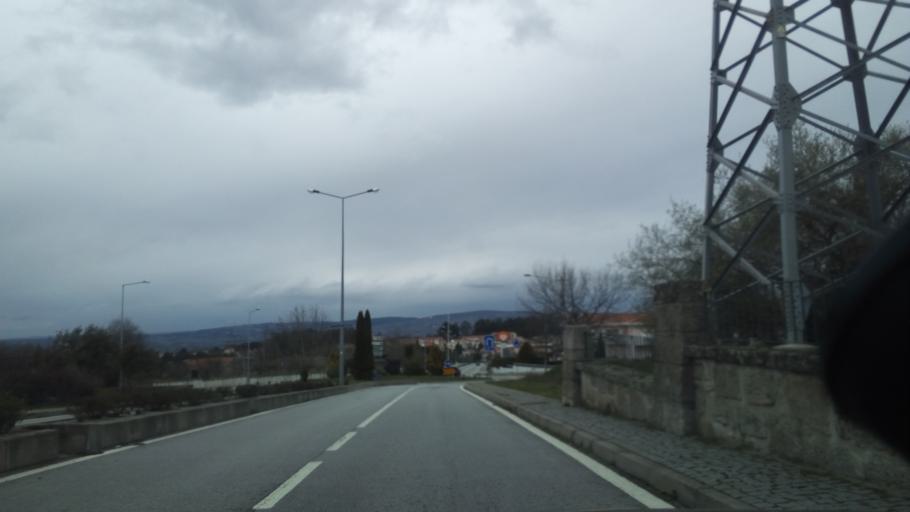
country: PT
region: Guarda
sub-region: Manteigas
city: Manteigas
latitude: 40.4961
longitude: -7.6023
